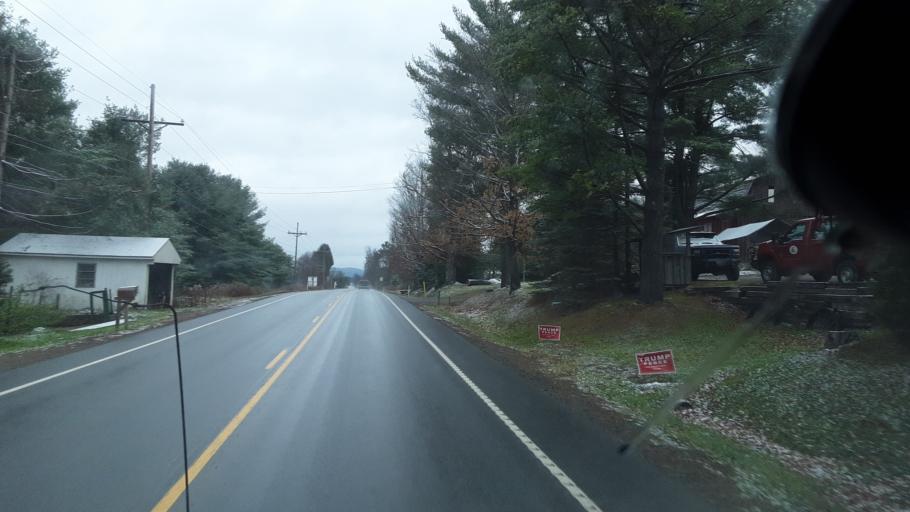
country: US
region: Pennsylvania
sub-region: Potter County
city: Shinglehouse
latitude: 41.9511
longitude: -78.1679
